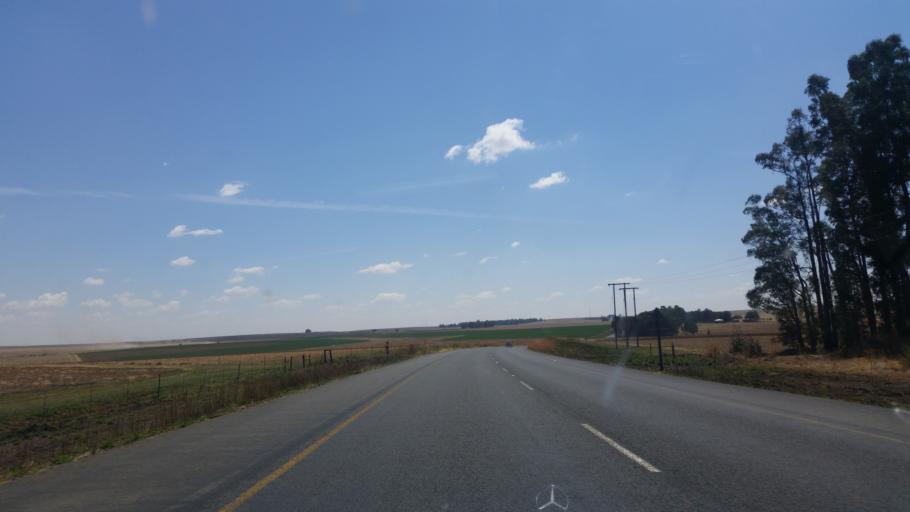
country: ZA
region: Orange Free State
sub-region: Thabo Mofutsanyana District Municipality
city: Bethlehem
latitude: -28.1041
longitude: 28.6605
